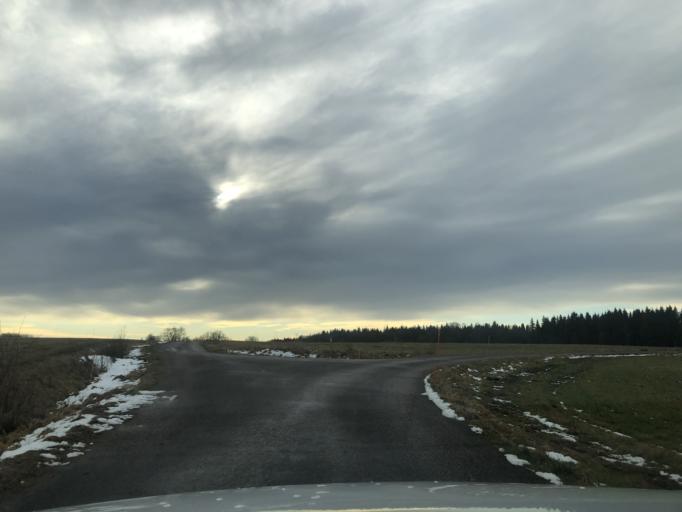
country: SE
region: Vaestra Goetaland
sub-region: Ulricehamns Kommun
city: Ulricehamn
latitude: 57.8171
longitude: 13.5302
